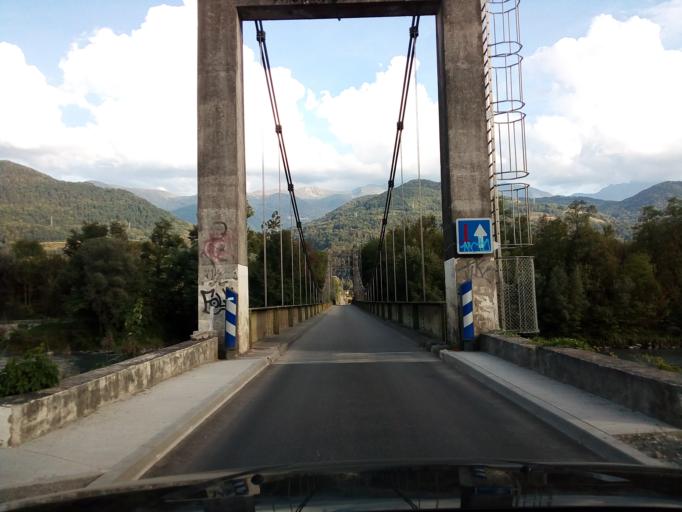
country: FR
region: Rhone-Alpes
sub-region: Departement de l'Isere
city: Tencin
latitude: 45.3163
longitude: 5.9446
